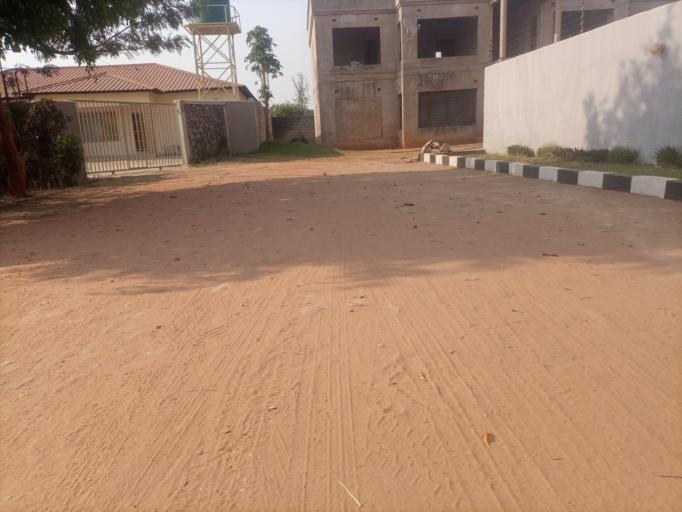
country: ZM
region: Lusaka
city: Lusaka
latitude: -15.4002
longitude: 28.3895
